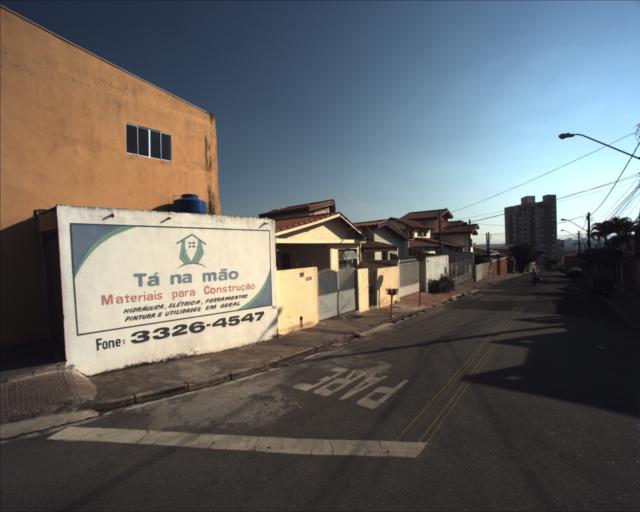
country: BR
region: Sao Paulo
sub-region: Sorocaba
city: Sorocaba
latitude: -23.4948
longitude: -47.4238
